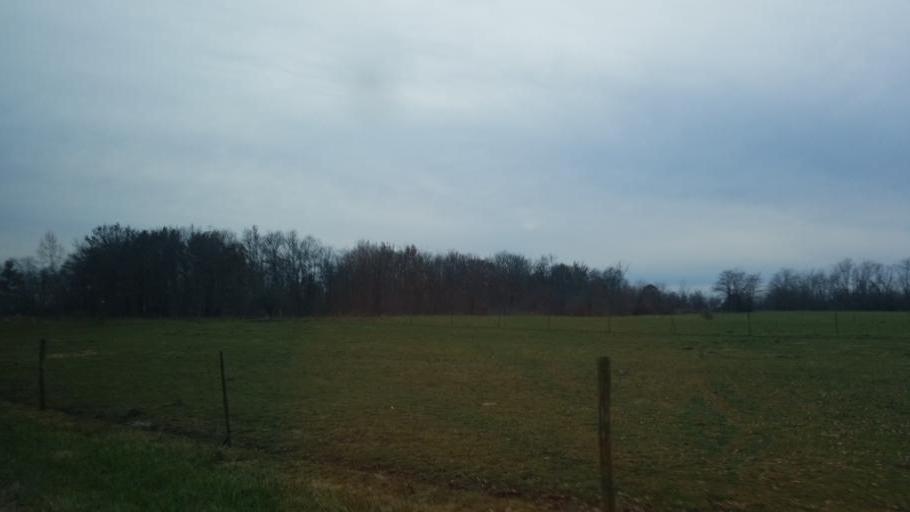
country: US
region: Indiana
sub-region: Adams County
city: Berne
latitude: 40.6635
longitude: -84.8595
